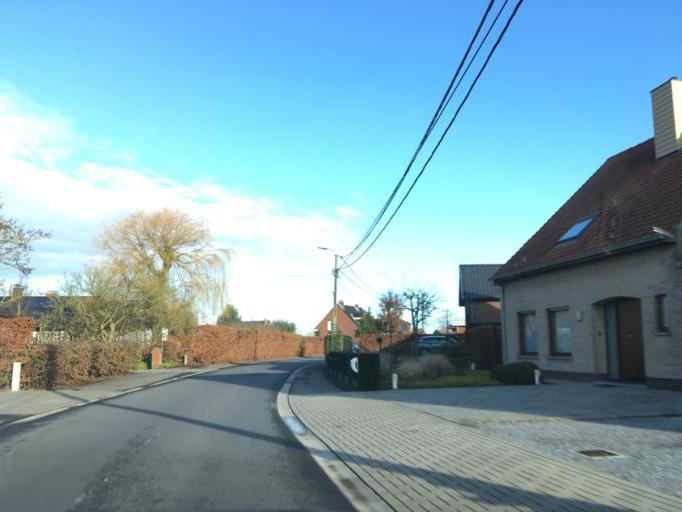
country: BE
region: Flanders
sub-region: Provincie West-Vlaanderen
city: Roeselare
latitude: 50.9172
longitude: 3.1450
